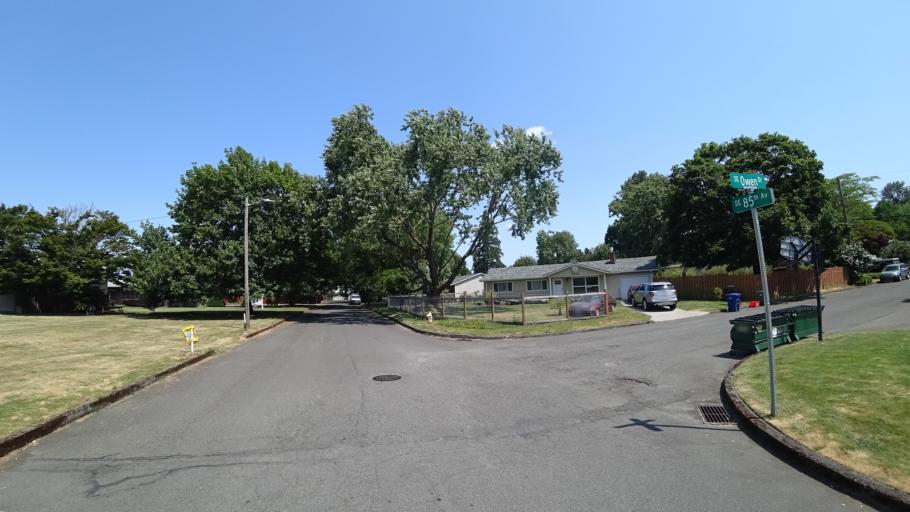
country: US
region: Oregon
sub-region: Multnomah County
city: Lents
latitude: 45.4448
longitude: -122.5761
